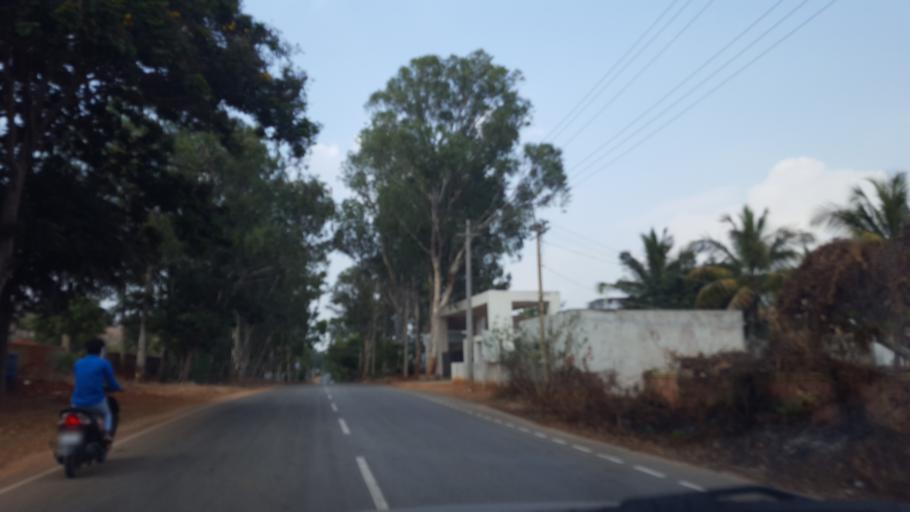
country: IN
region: Karnataka
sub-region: Chikkaballapur
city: Chik Ballapur
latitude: 13.3677
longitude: 77.6962
